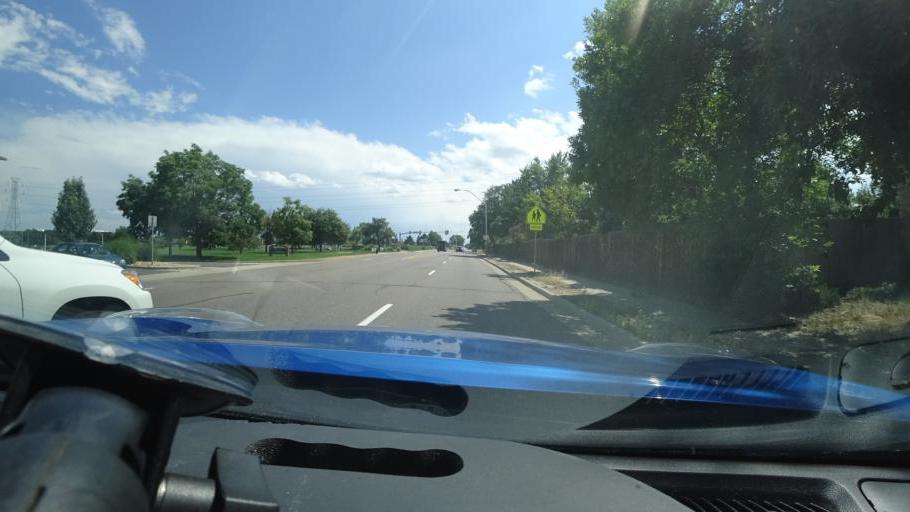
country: US
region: Colorado
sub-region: Adams County
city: Aurora
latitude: 39.6833
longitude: -104.8473
